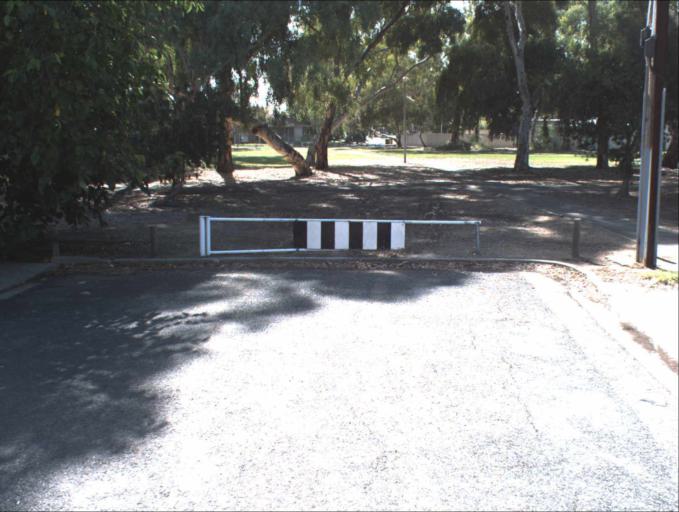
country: AU
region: South Australia
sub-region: Prospect
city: Prospect
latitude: -34.8768
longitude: 138.5752
